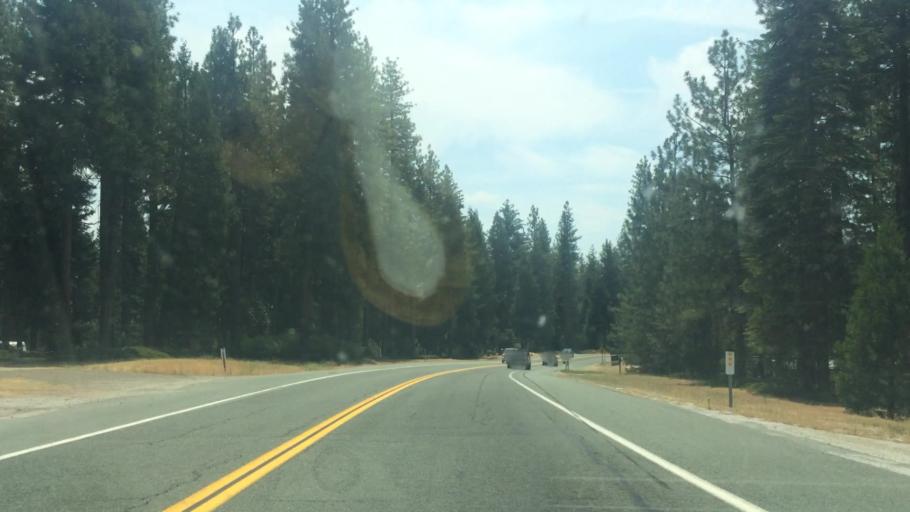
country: US
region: California
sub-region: Amador County
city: Pioneer
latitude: 38.4849
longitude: -120.5184
